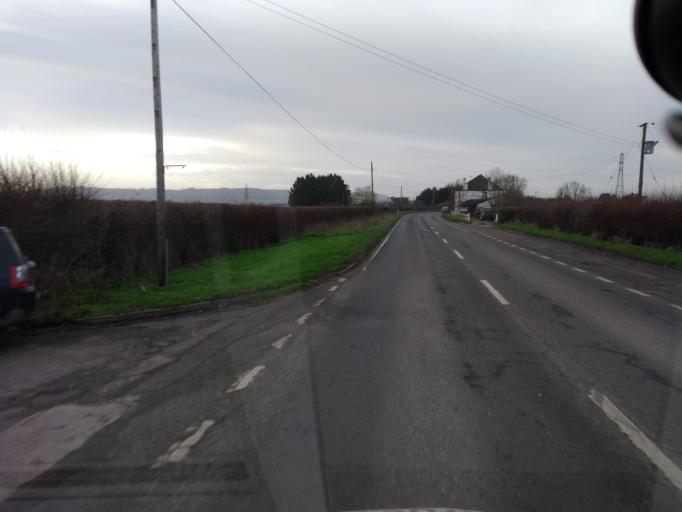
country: GB
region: England
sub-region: Somerset
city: Westonzoyland
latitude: 51.1141
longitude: -2.8526
